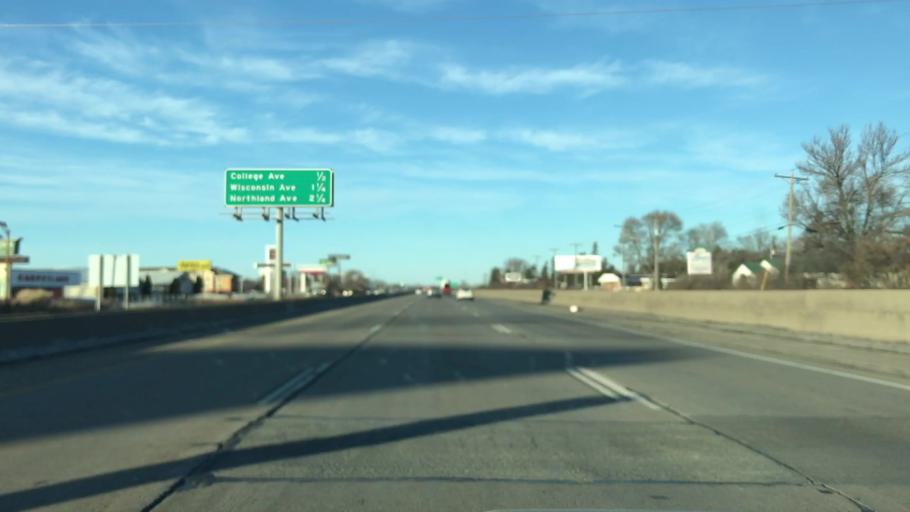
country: US
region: Wisconsin
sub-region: Outagamie County
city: Appleton
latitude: 44.2512
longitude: -88.4663
